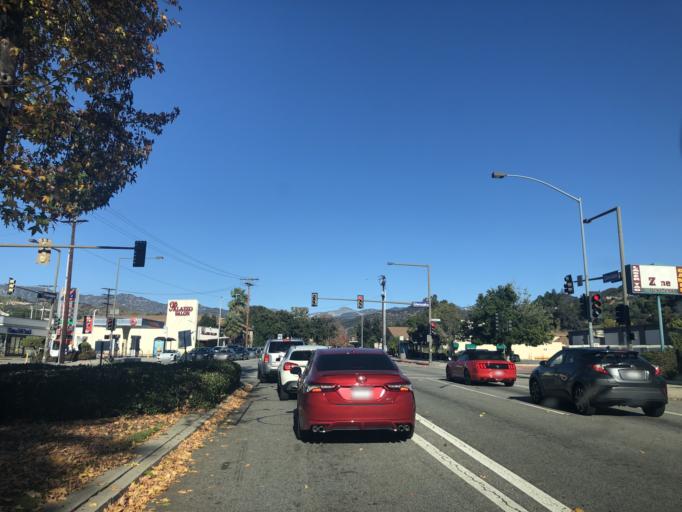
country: US
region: California
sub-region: Los Angeles County
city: Glendale
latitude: 34.1584
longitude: -118.2401
